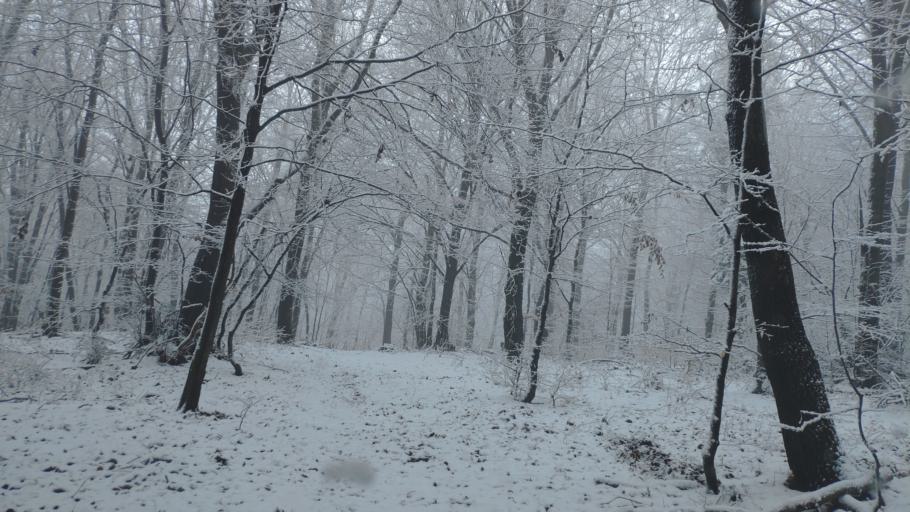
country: SK
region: Kosicky
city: Moldava nad Bodvou
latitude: 48.7392
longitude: 21.0935
